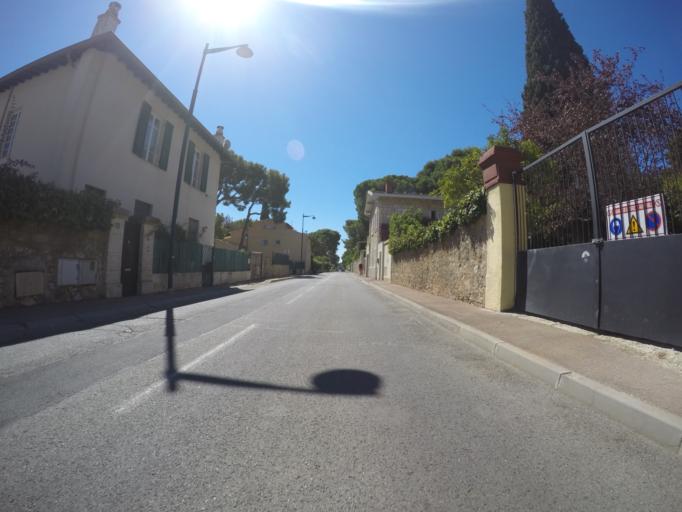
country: FR
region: Provence-Alpes-Cote d'Azur
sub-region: Departement des Alpes-Maritimes
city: Saint-Jean-Cap-Ferrat
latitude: 43.6854
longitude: 7.3315
